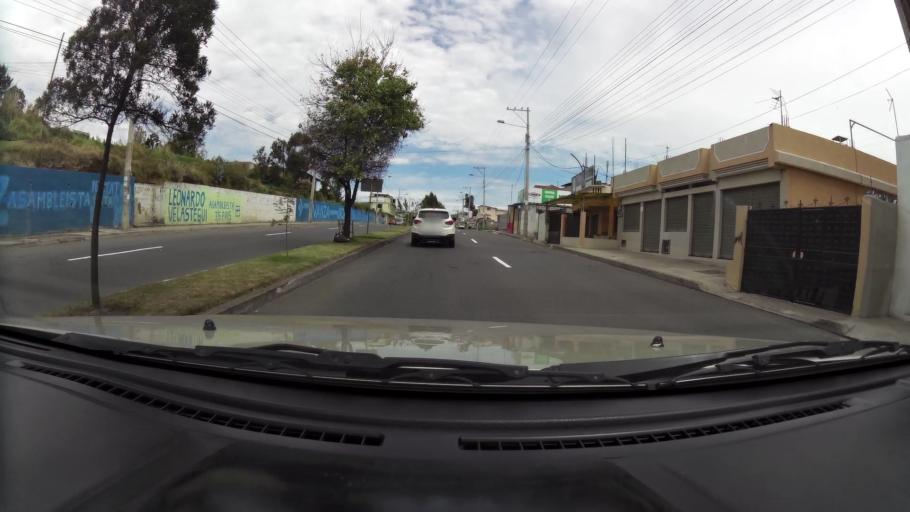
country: EC
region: Cotopaxi
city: San Miguel de Salcedo
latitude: -1.0839
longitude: -78.5944
